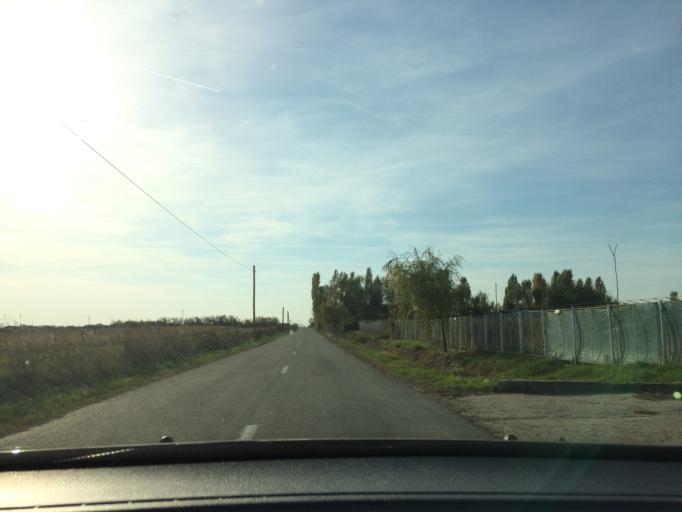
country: RO
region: Timis
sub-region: Oras Recas
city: Recas
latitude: 45.8082
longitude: 21.5337
